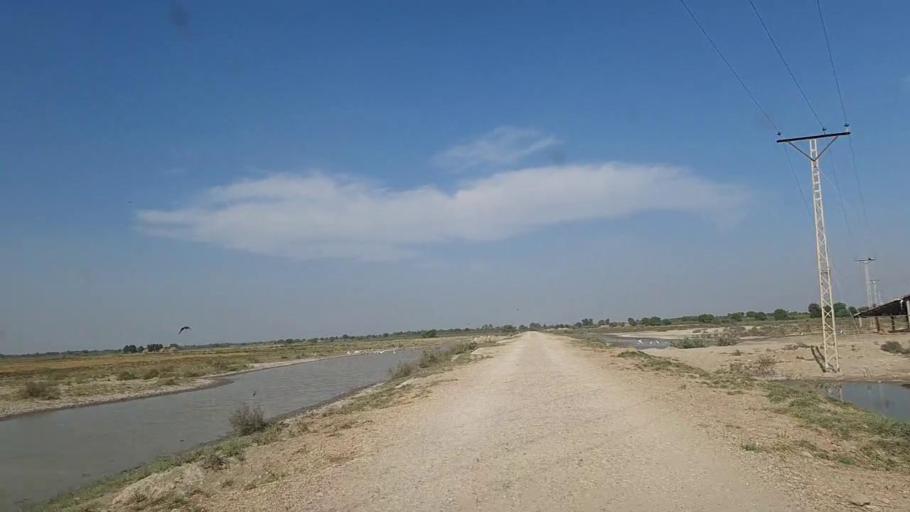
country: PK
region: Sindh
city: Bulri
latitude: 24.8687
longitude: 68.2671
